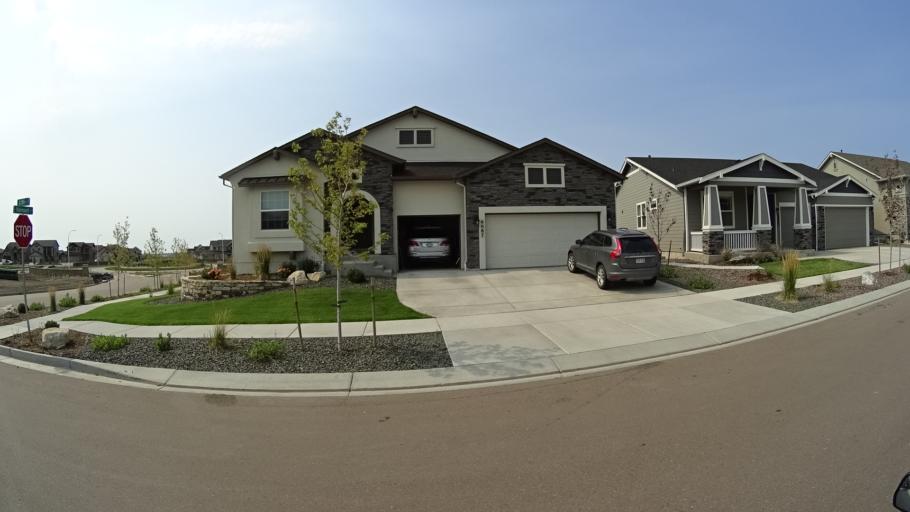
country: US
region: Colorado
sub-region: El Paso County
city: Black Forest
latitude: 38.9734
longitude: -104.7221
